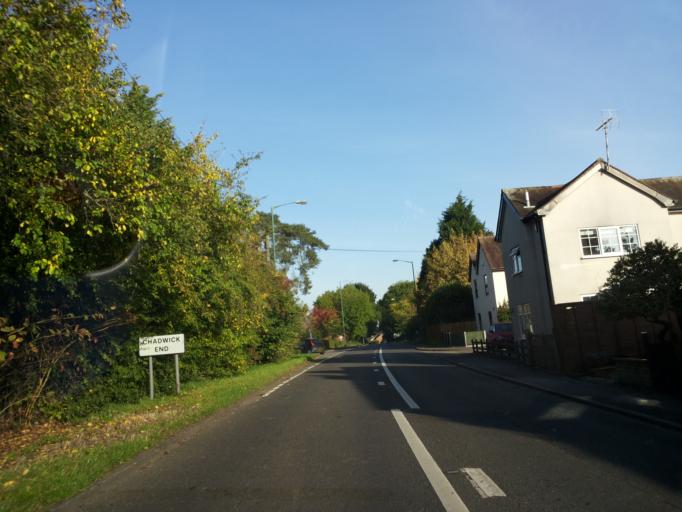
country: GB
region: England
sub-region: Warwickshire
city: Wroxall
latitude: 52.3509
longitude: -1.6943
